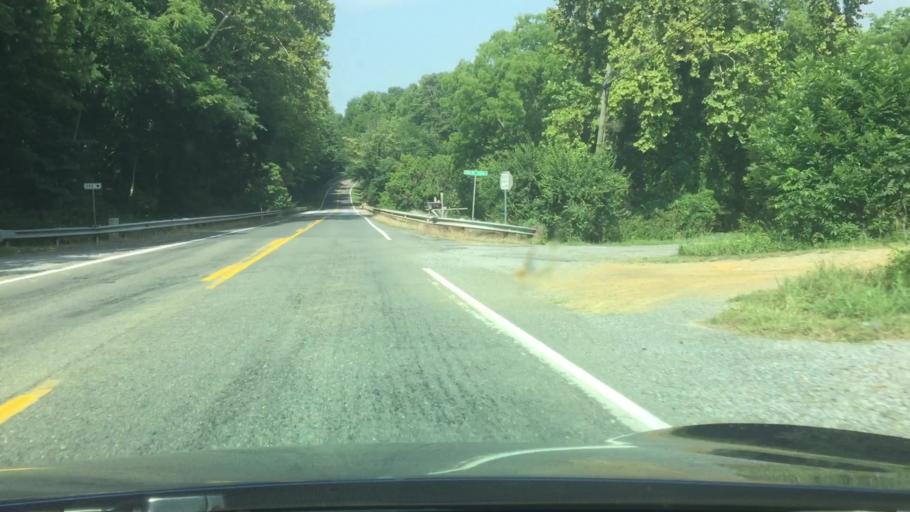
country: US
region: Virginia
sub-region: Pulaski County
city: Pulaski
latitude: 36.9491
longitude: -80.9145
